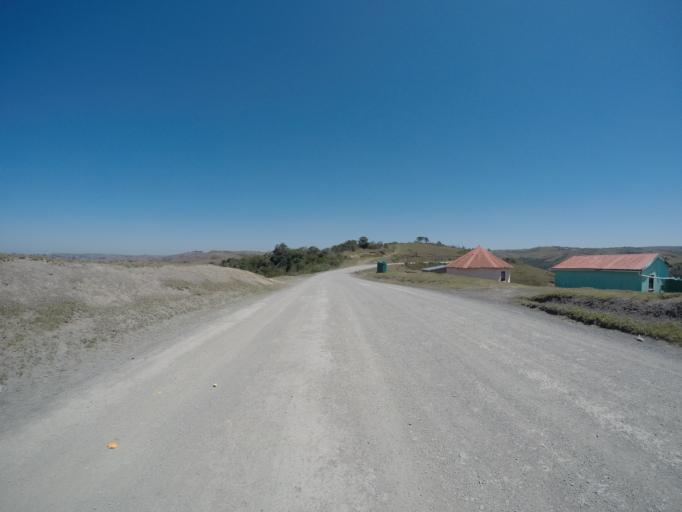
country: ZA
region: Eastern Cape
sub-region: OR Tambo District Municipality
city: Libode
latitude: -31.9995
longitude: 29.0683
